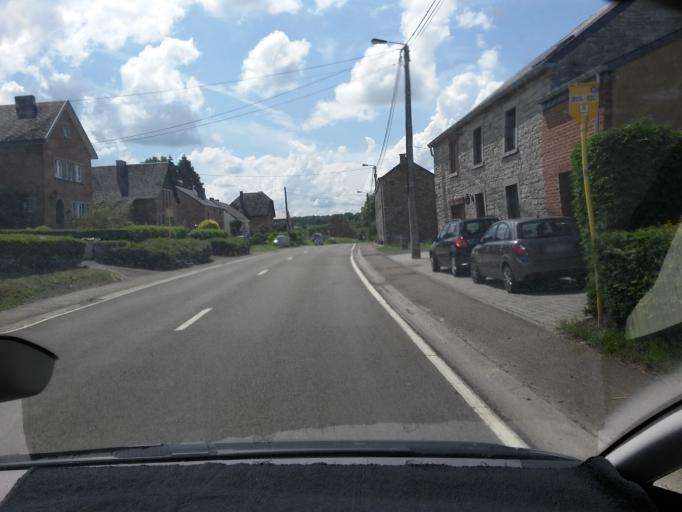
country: BE
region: Wallonia
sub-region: Province de Namur
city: Rochefort
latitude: 50.1307
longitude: 5.2716
